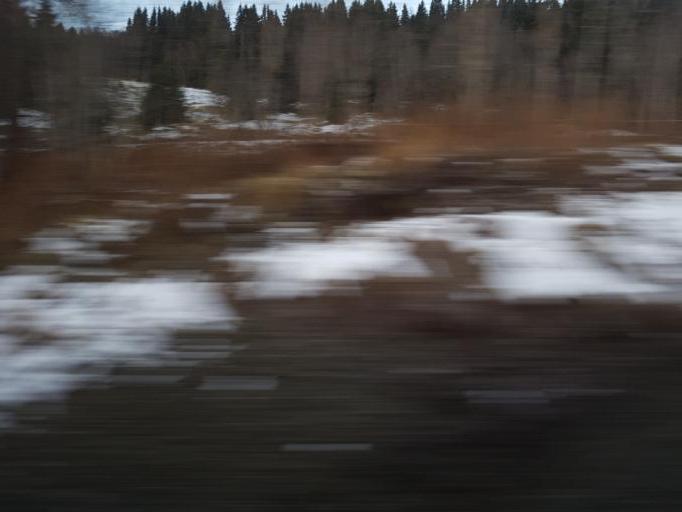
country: NO
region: Sor-Trondelag
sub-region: Midtre Gauldal
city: Storen
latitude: 62.9526
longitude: 10.1887
